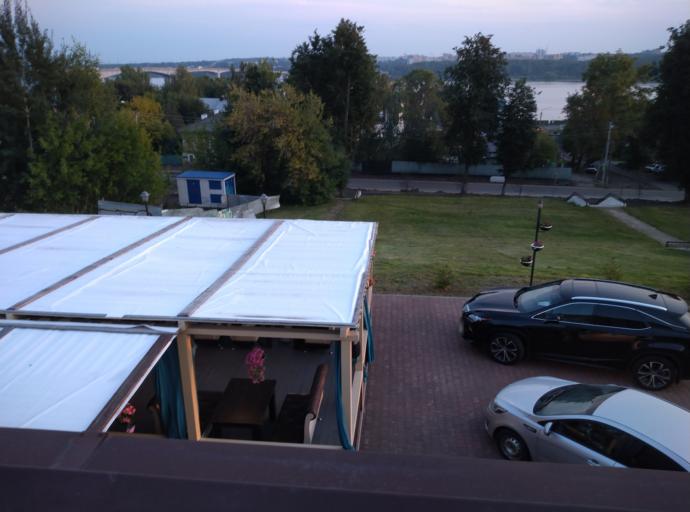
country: RU
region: Kostroma
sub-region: Kostromskoy Rayon
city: Kostroma
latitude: 57.7595
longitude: 40.9412
